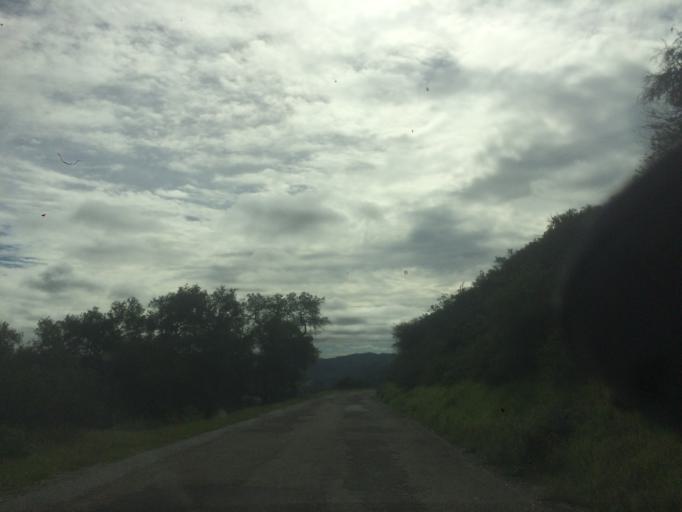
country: US
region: California
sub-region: San Luis Obispo County
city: Nipomo
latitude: 35.1981
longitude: -120.4465
